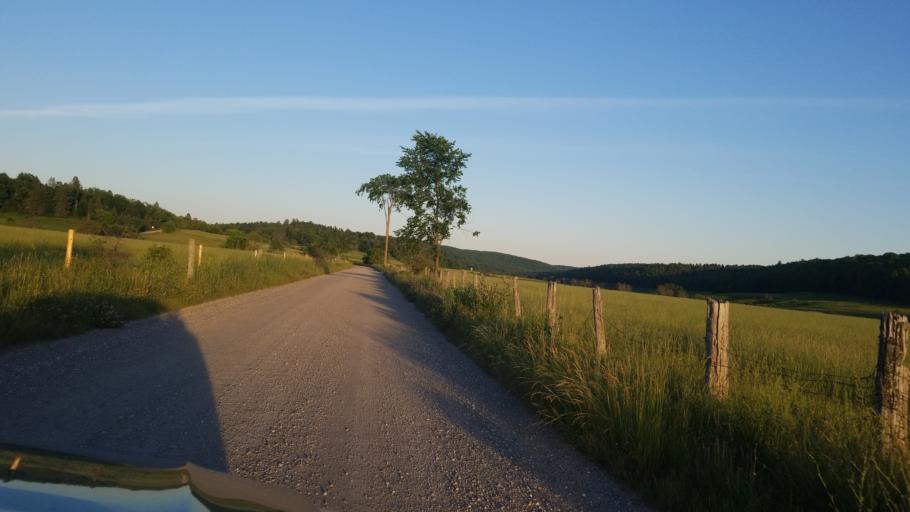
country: CA
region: Quebec
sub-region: Outaouais
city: Wakefield
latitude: 45.5841
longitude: -75.9001
